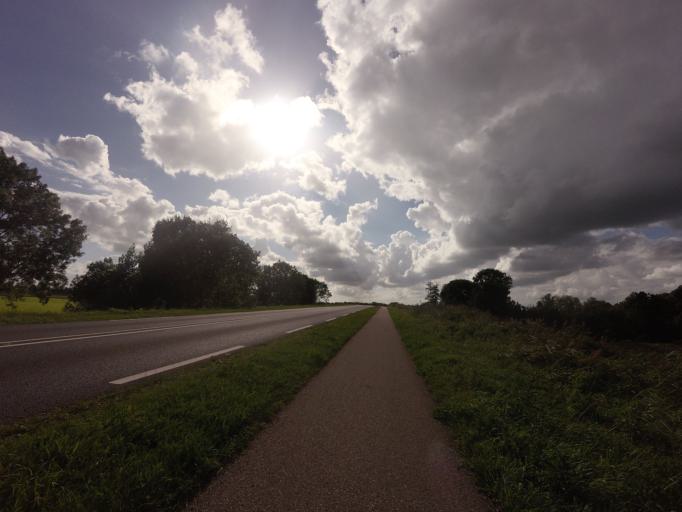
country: NL
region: Overijssel
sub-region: Gemeente Steenwijkerland
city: Blokzijl
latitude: 52.7447
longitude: 5.9987
